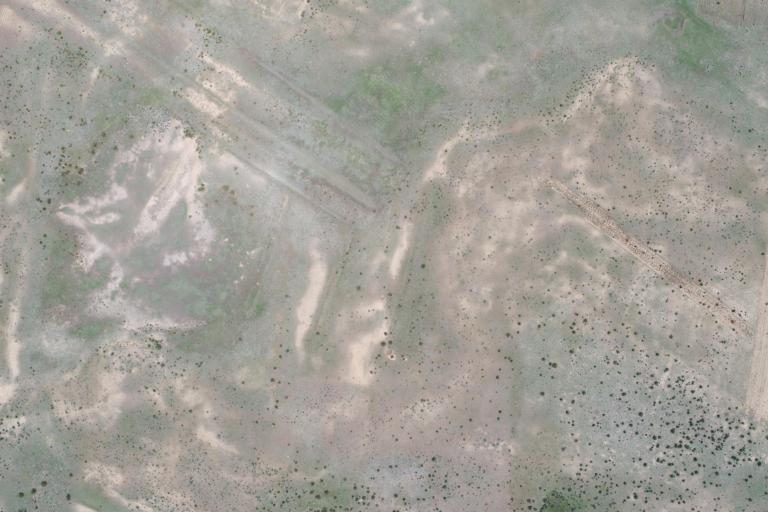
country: BO
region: La Paz
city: Curahuara de Carangas
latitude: -17.2776
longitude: -68.5177
